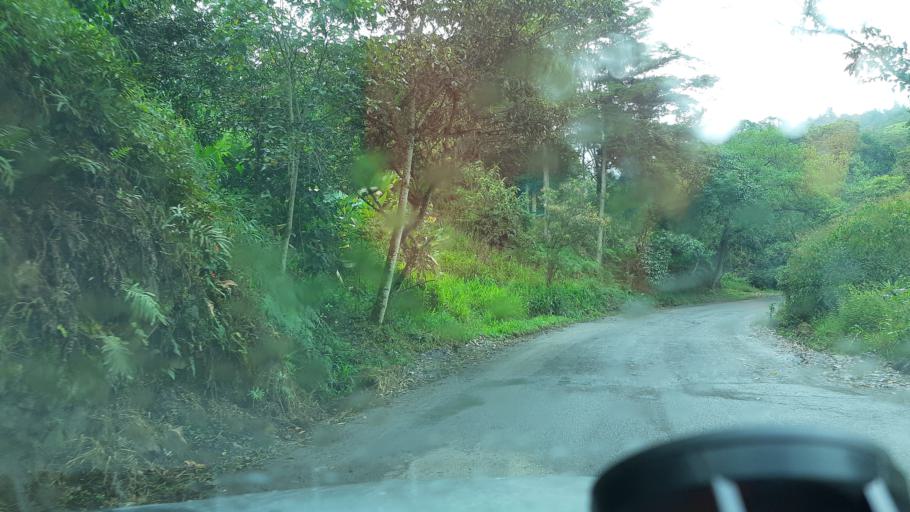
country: CO
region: Boyaca
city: Chinavita
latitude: 5.1520
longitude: -73.3625
